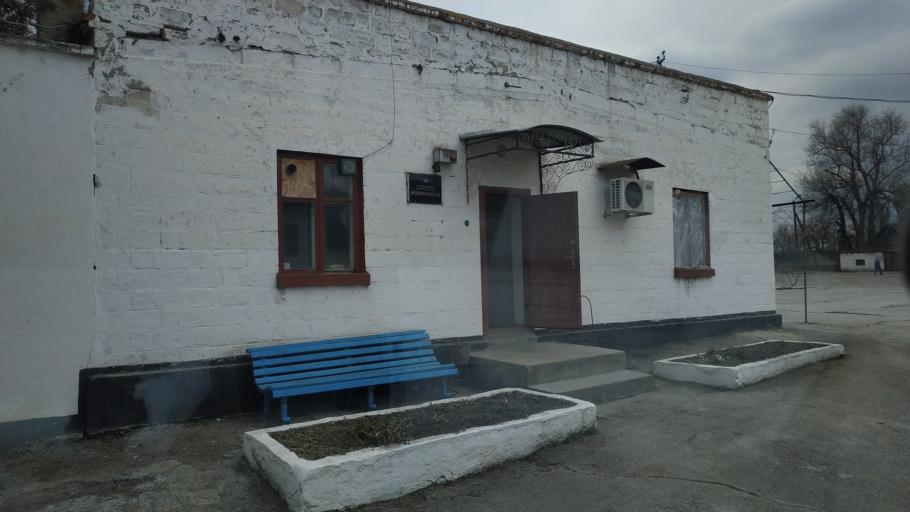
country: MD
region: Anenii Noi
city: Anenii Noi
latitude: 46.8896
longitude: 29.2948
